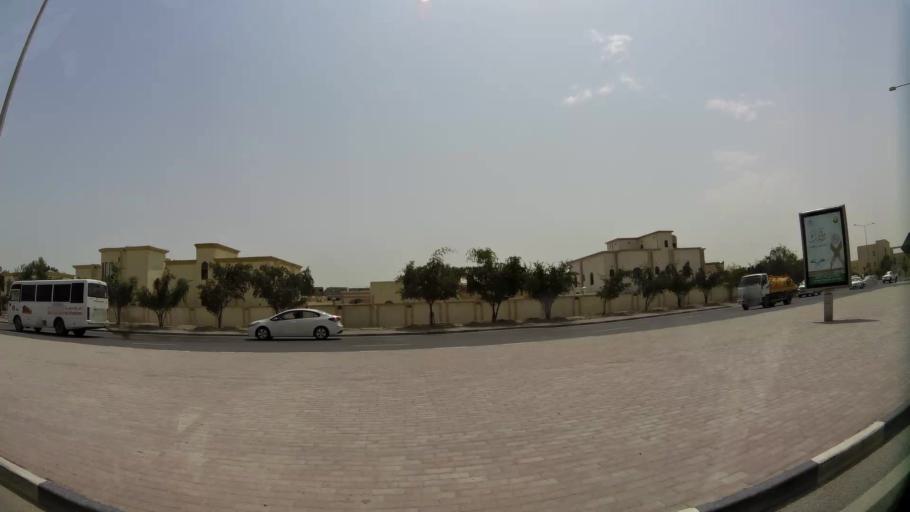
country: QA
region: Baladiyat ar Rayyan
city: Ar Rayyan
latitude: 25.2463
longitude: 51.4207
